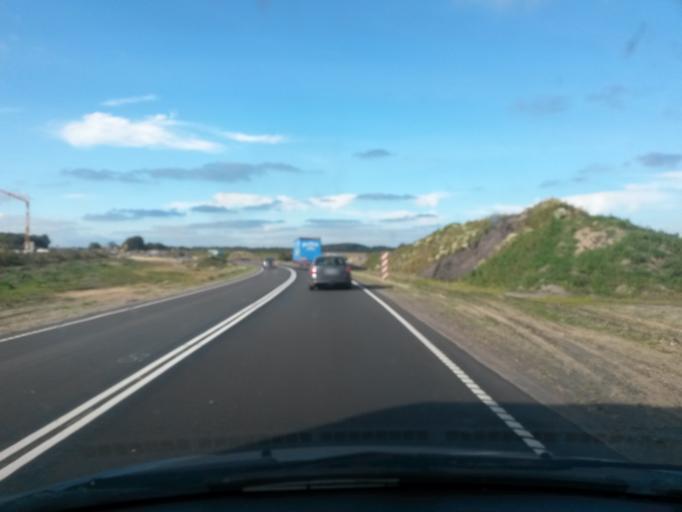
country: DK
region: Central Jutland
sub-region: Herning Kommune
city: Avlum
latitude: 56.2918
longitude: 8.7325
